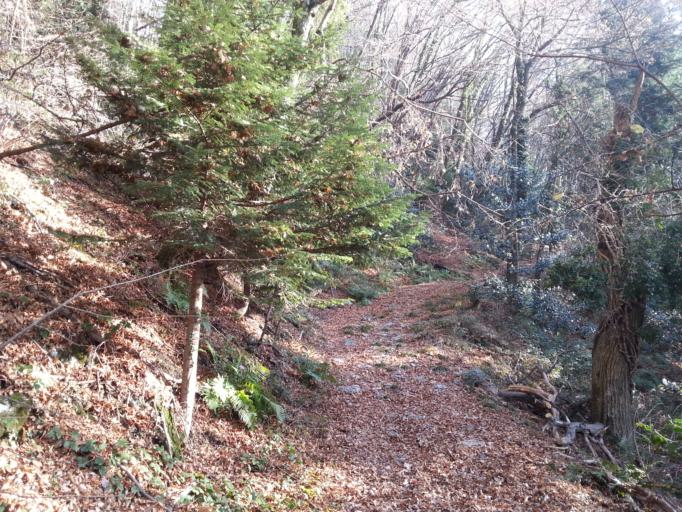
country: IT
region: Lombardy
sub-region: Provincia di Como
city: Maslianico
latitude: 45.8586
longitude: 9.0451
